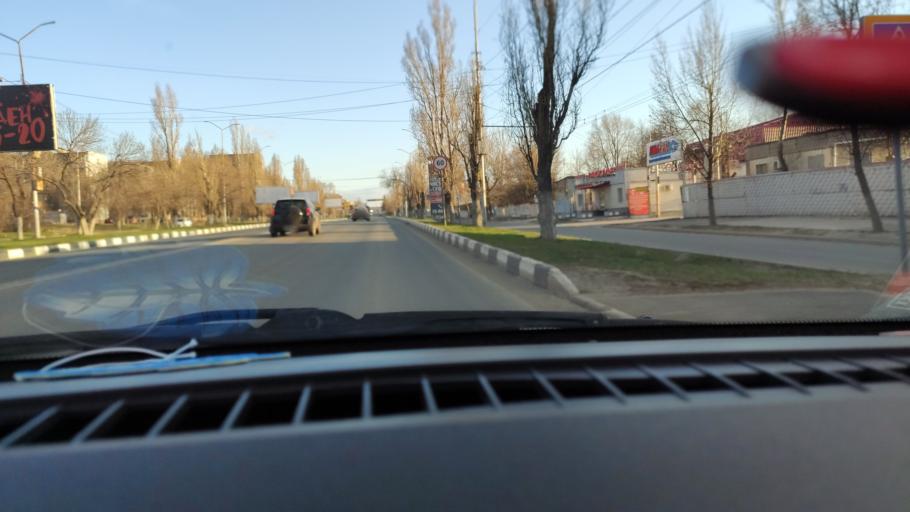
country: RU
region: Saratov
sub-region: Saratovskiy Rayon
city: Saratov
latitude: 51.6047
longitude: 45.9689
